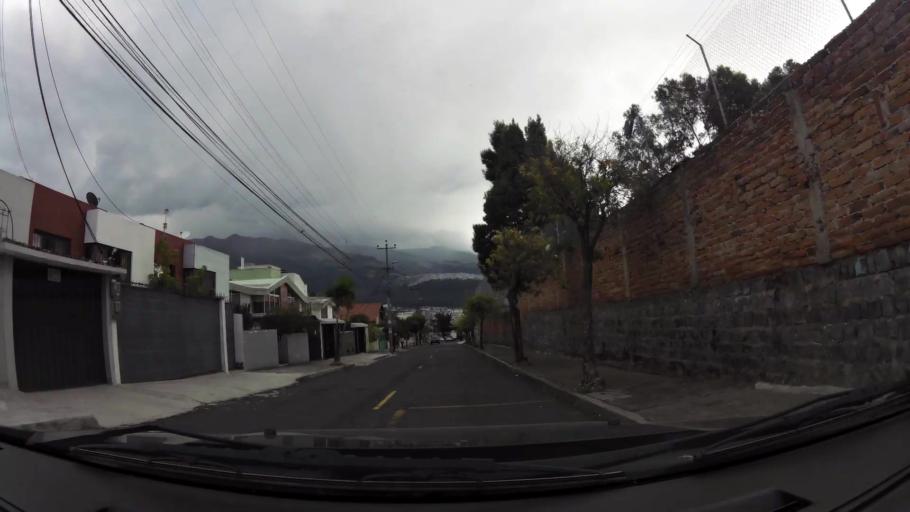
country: EC
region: Pichincha
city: Quito
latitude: -0.1317
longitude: -78.4850
